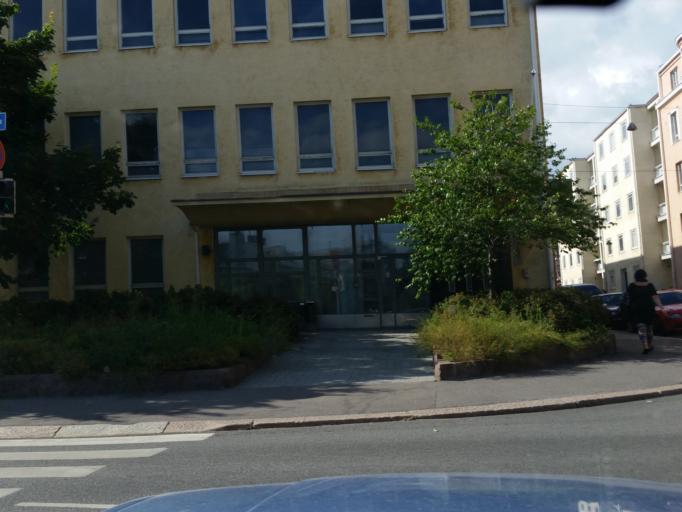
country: FI
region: Uusimaa
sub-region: Helsinki
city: Helsinki
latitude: 60.1633
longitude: 24.9302
